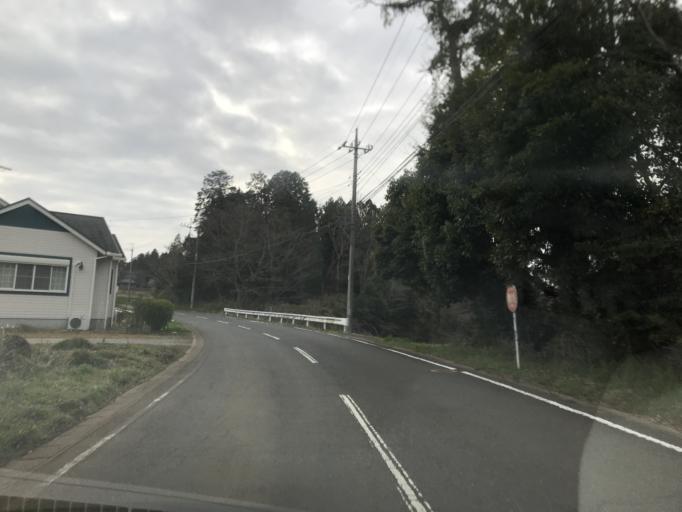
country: JP
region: Chiba
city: Sawara
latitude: 35.8115
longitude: 140.5377
